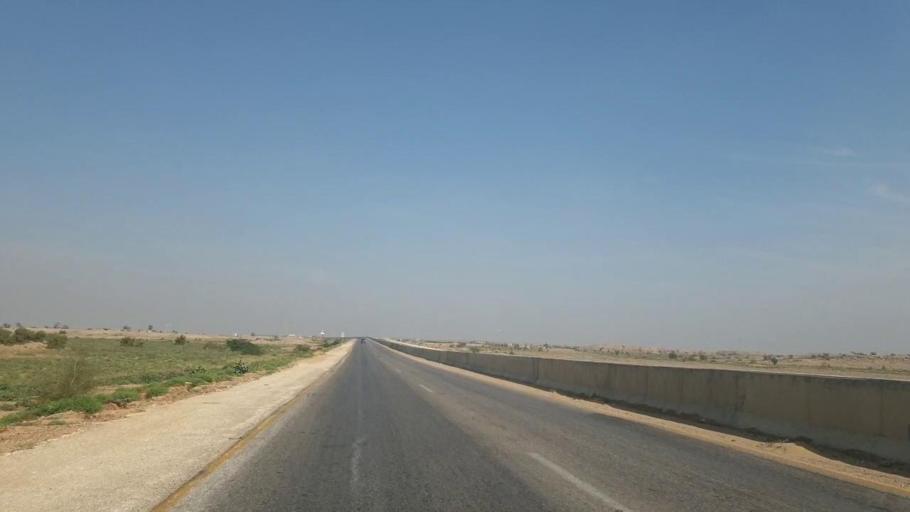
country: PK
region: Sindh
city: Jamshoro
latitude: 25.5636
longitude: 68.3090
